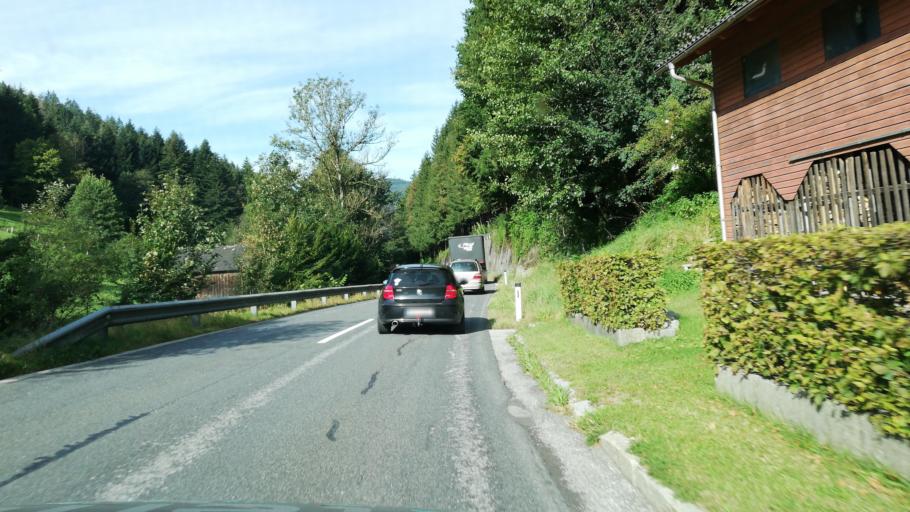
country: AT
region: Lower Austria
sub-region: Politischer Bezirk Amstetten
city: Behamberg
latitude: 47.9927
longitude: 14.5195
